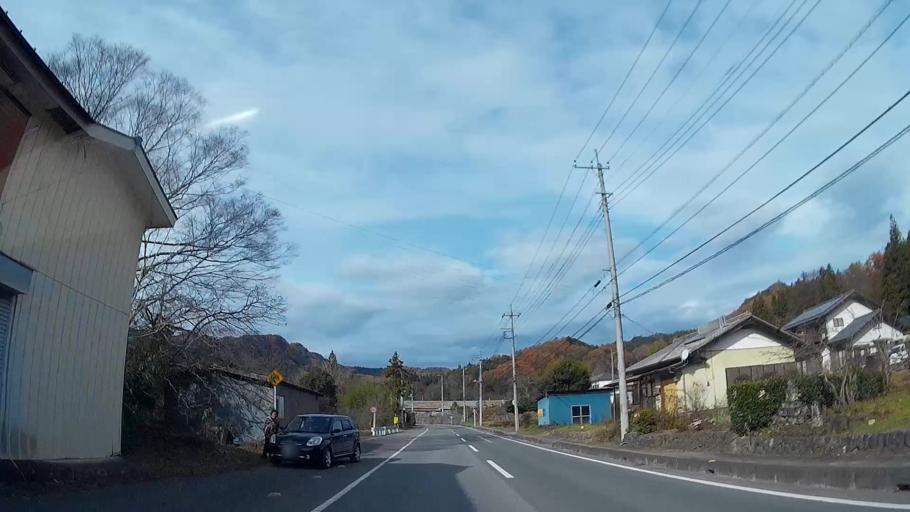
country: JP
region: Saitama
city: Chichibu
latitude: 36.0452
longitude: 138.9930
